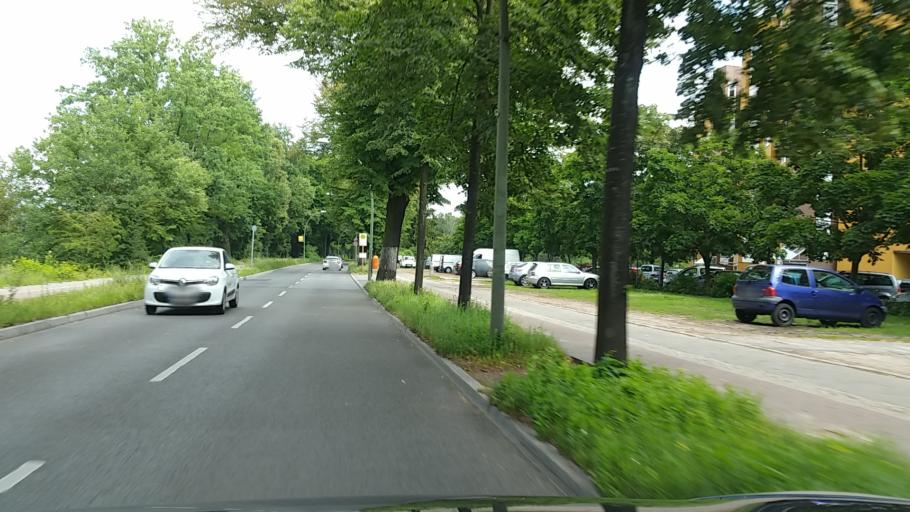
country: DE
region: Berlin
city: Siemensstadt
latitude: 52.5485
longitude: 13.2636
